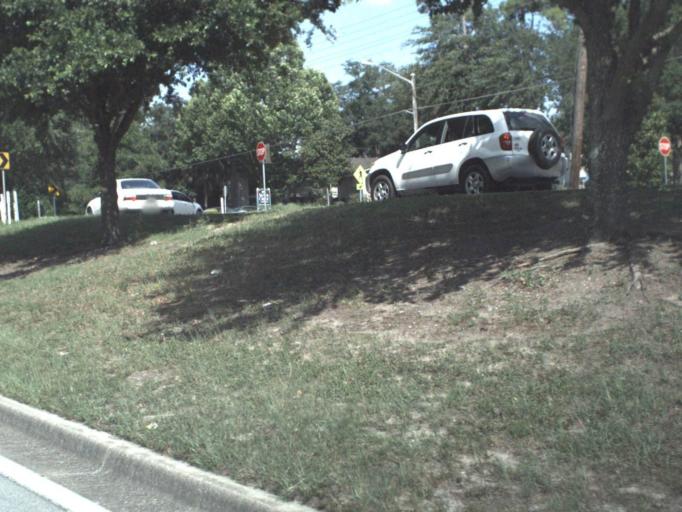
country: US
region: Florida
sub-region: Alachua County
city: Gainesville
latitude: 29.6288
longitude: -82.3688
